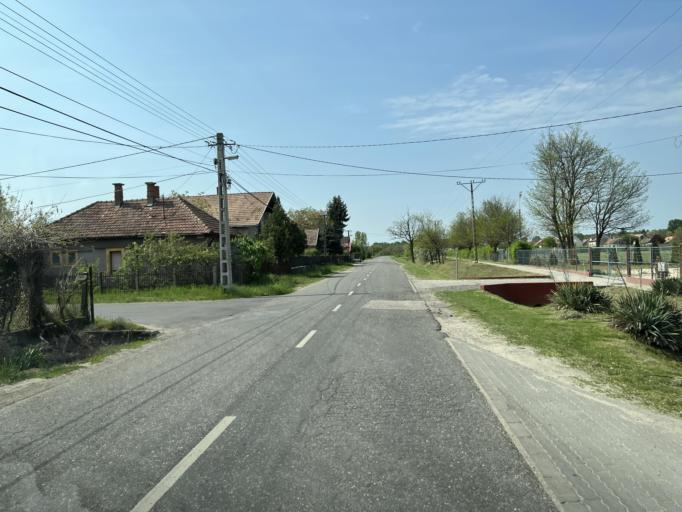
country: HU
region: Pest
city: Tortel
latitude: 47.1176
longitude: 19.9237
